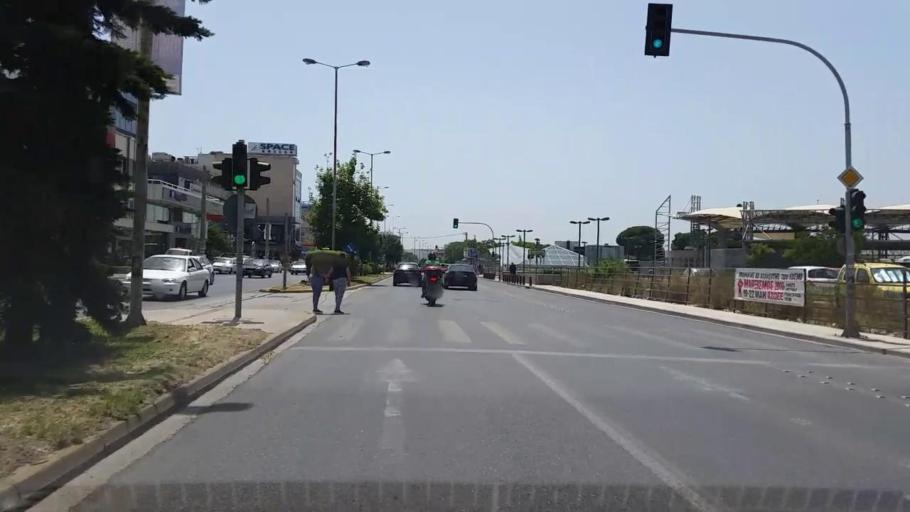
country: GR
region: Attica
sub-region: Nomarchia Athinas
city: Cholargos
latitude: 38.0098
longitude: 23.8072
